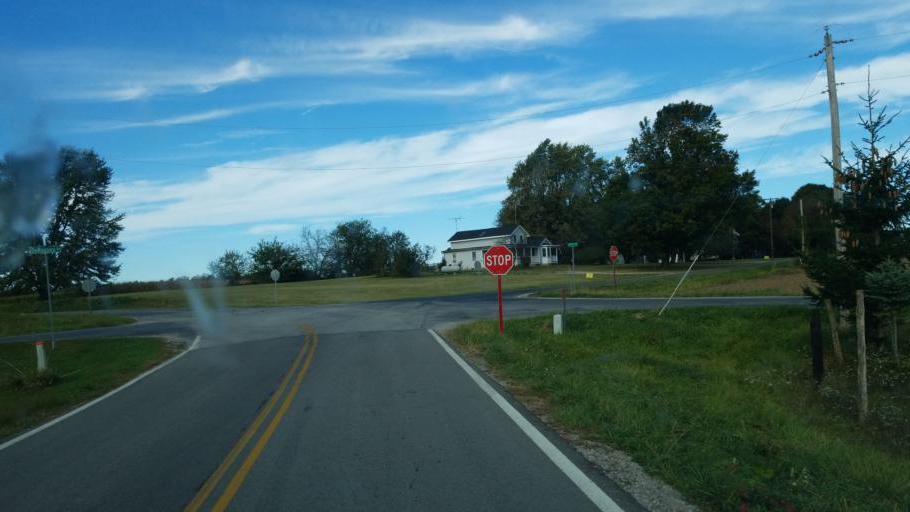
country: US
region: Ohio
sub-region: Huron County
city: Wakeman
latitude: 41.1746
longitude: -82.4577
